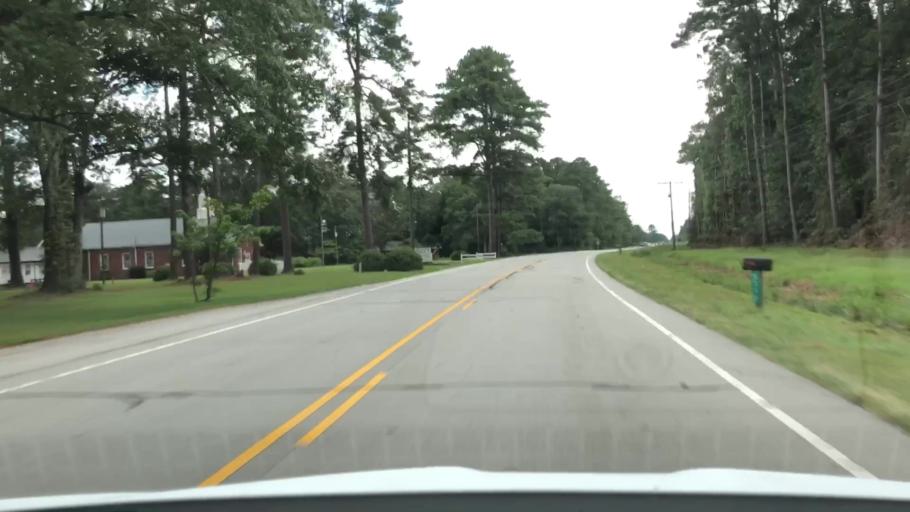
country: US
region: North Carolina
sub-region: Lenoir County
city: Kinston
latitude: 35.1207
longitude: -77.5168
